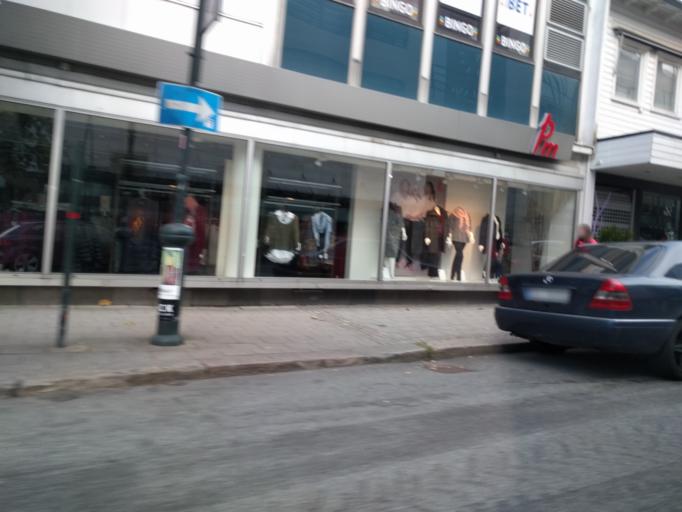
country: NO
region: Vest-Agder
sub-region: Kristiansand
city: Kristiansand
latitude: 58.1467
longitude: 7.9909
